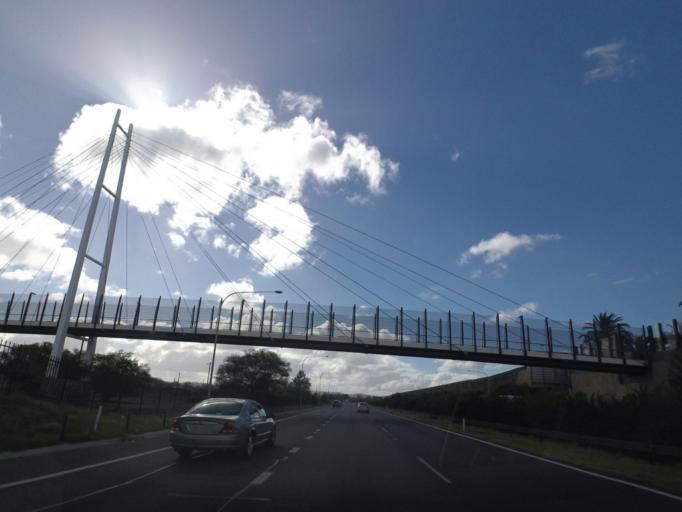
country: AU
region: New South Wales
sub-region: Albury Municipality
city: East Albury
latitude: -36.0823
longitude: 146.9259
